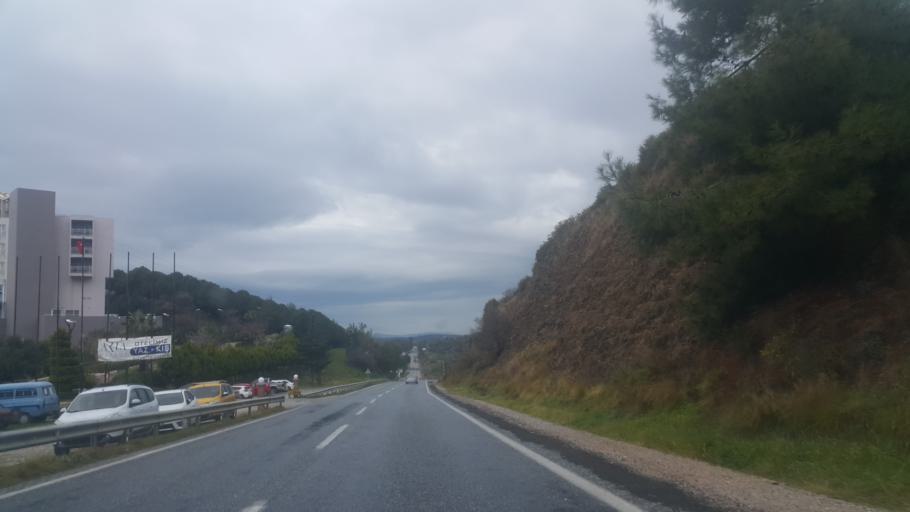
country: TR
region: Izmir
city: Ozdere
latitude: 37.9902
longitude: 27.1407
